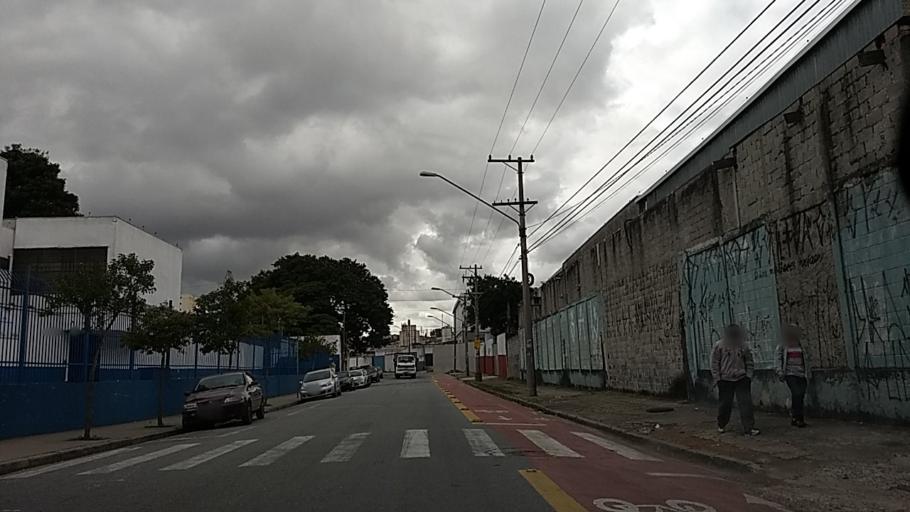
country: BR
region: Sao Paulo
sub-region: Sao Paulo
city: Sao Paulo
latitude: -23.5122
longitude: -46.6087
